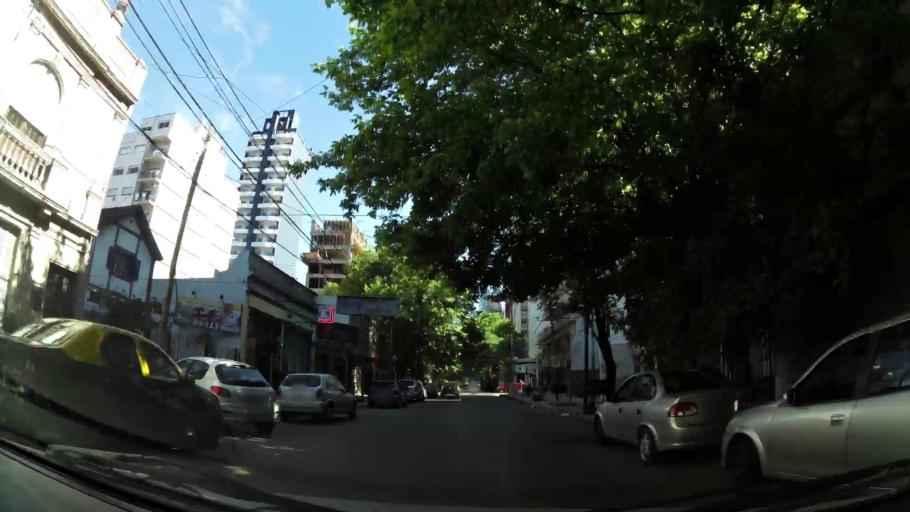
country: AR
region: Buenos Aires
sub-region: Partido de Lomas de Zamora
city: Lomas de Zamora
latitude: -34.7609
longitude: -58.4041
